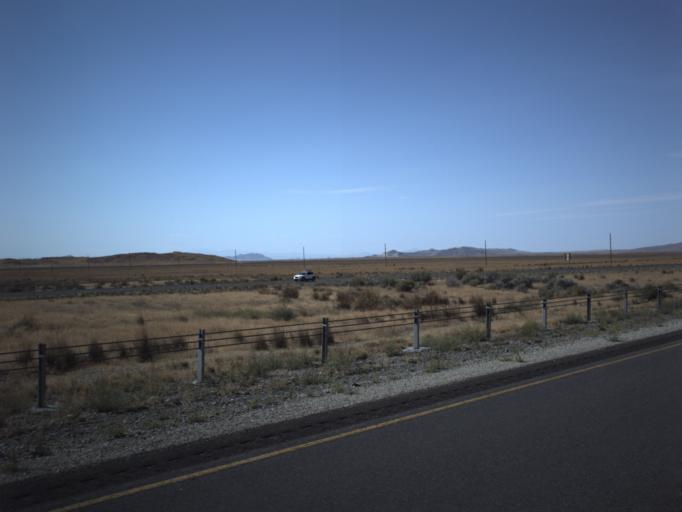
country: US
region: Utah
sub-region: Tooele County
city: Grantsville
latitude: 40.7265
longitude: -113.1373
